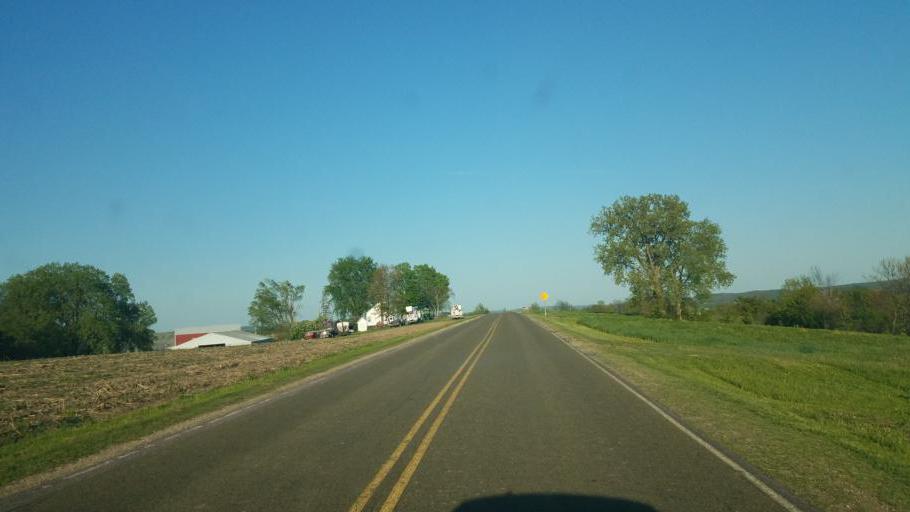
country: US
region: Wisconsin
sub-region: Vernon County
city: Hillsboro
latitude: 43.6438
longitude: -90.2757
